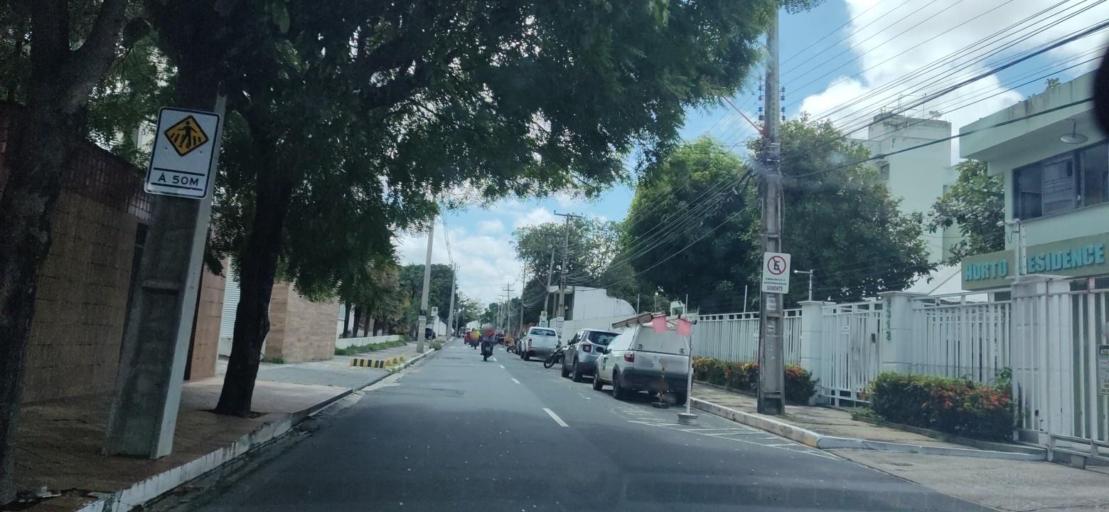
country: BR
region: Piaui
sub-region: Teresina
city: Teresina
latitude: -5.0650
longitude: -42.7822
